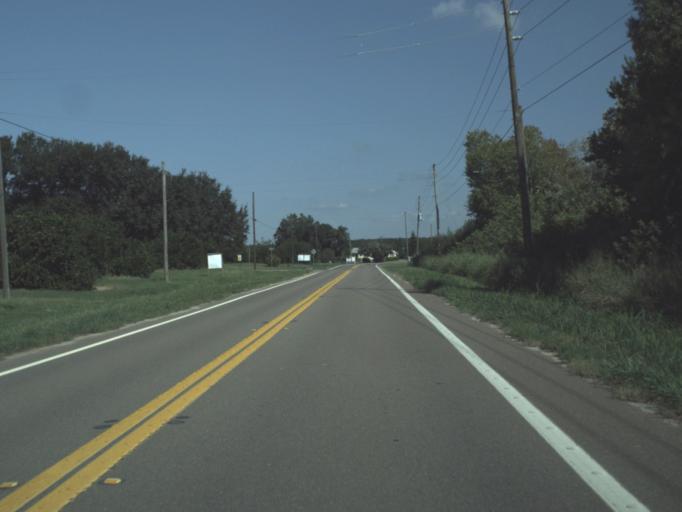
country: US
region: Florida
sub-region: Polk County
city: Frostproof
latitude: 27.7767
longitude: -81.5378
